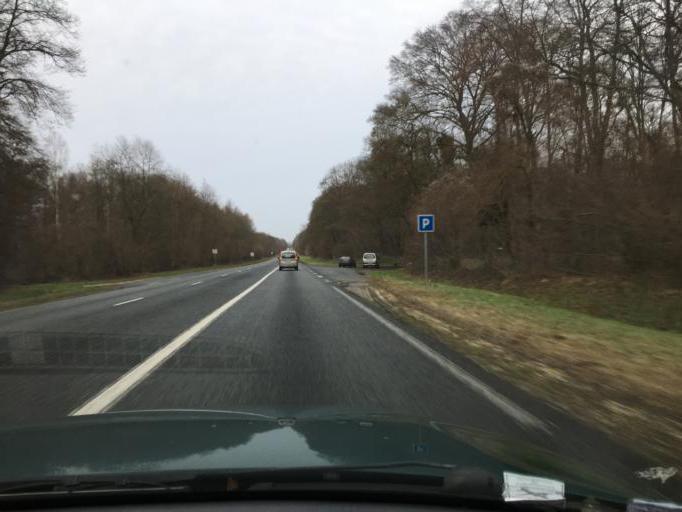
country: FR
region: Picardie
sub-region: Departement de l'Oise
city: Thiers-sur-Theve
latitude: 49.1736
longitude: 2.5619
